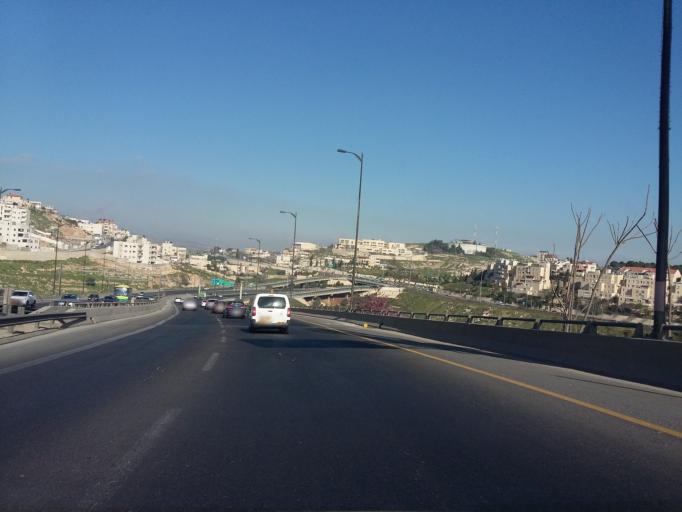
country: PS
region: West Bank
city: `Anata
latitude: 31.8155
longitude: 35.2376
